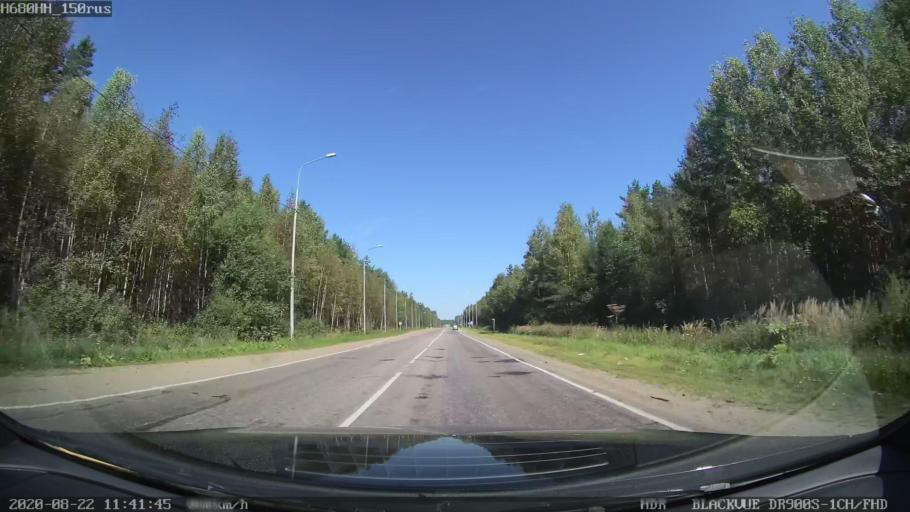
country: RU
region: Tverskaya
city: Sakharovo
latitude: 56.9929
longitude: 36.0252
